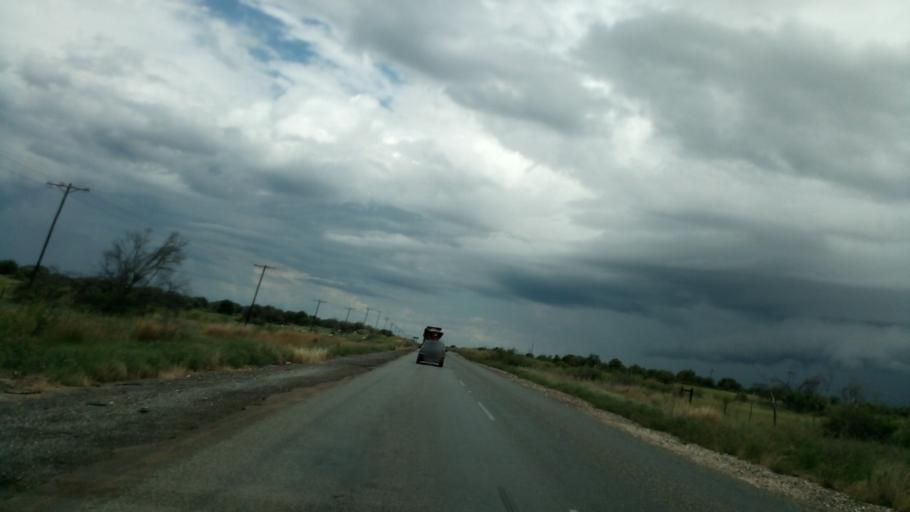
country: ZA
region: Northern Cape
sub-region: Frances Baard District Municipality
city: Barkly West
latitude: -28.2651
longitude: 24.0656
